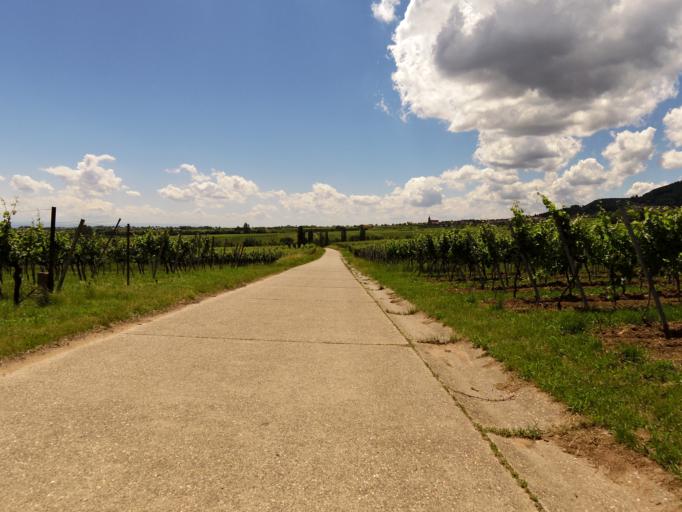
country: DE
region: Rheinland-Pfalz
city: Hainfeld
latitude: 49.2622
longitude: 8.0863
